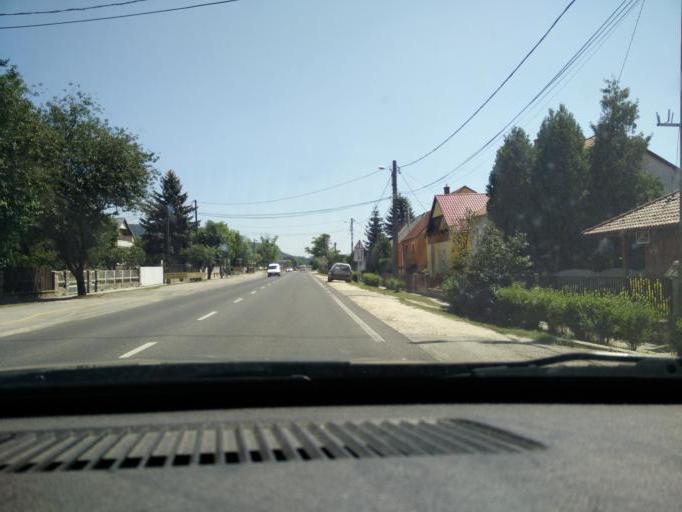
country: HU
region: Komarom-Esztergom
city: Vertesszolos
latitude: 47.6149
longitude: 18.3806
